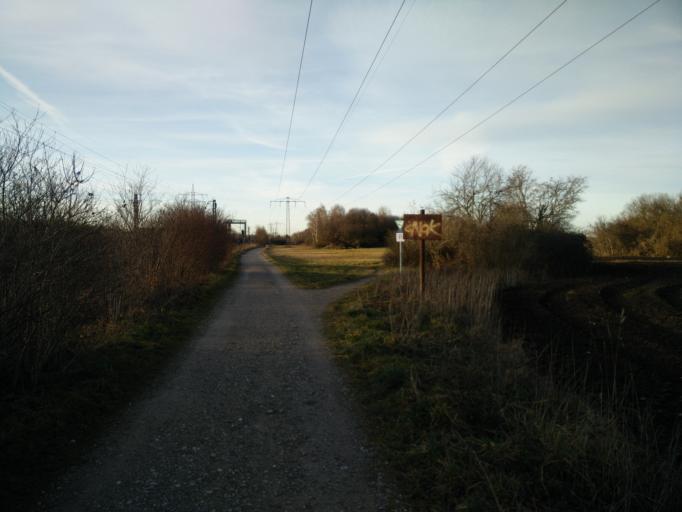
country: DE
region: Bavaria
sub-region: Upper Bavaria
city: Pasing
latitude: 48.1643
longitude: 11.4308
